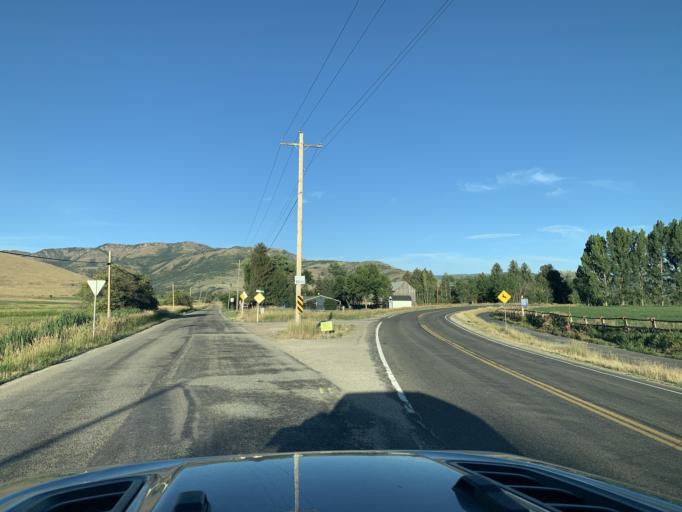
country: US
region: Utah
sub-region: Weber County
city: Wolf Creek
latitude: 41.2931
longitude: -111.7800
